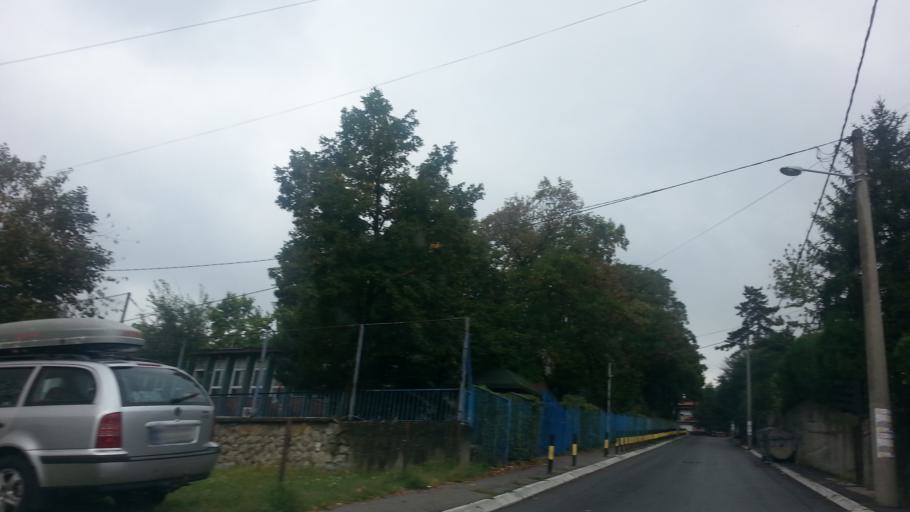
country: RS
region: Central Serbia
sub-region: Belgrade
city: Rakovica
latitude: 44.7466
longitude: 20.4416
